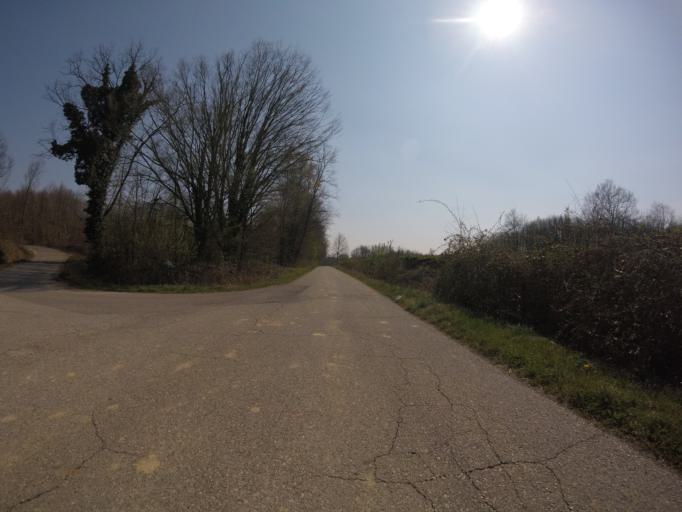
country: HR
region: Grad Zagreb
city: Strmec
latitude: 45.5677
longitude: 15.9208
